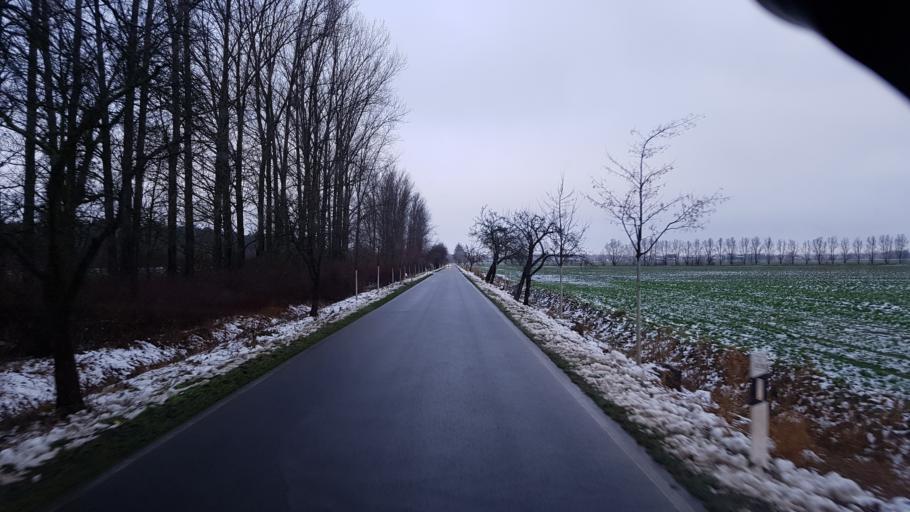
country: DE
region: Brandenburg
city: Luckau
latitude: 51.8088
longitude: 13.7154
